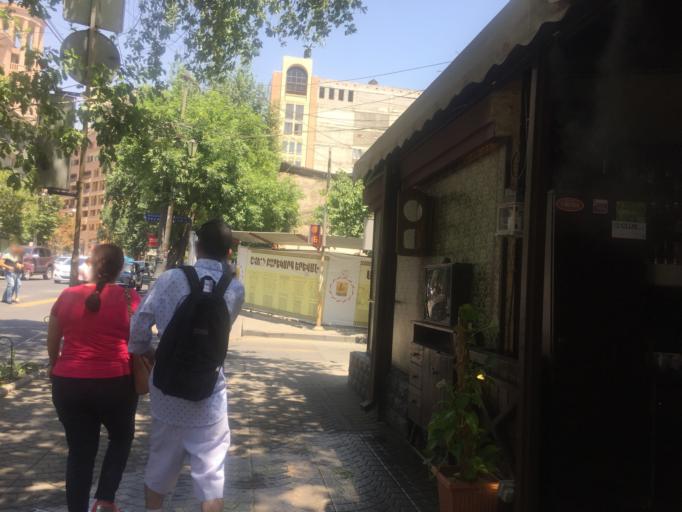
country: AM
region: Yerevan
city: Yerevan
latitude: 40.1794
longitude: 44.5138
